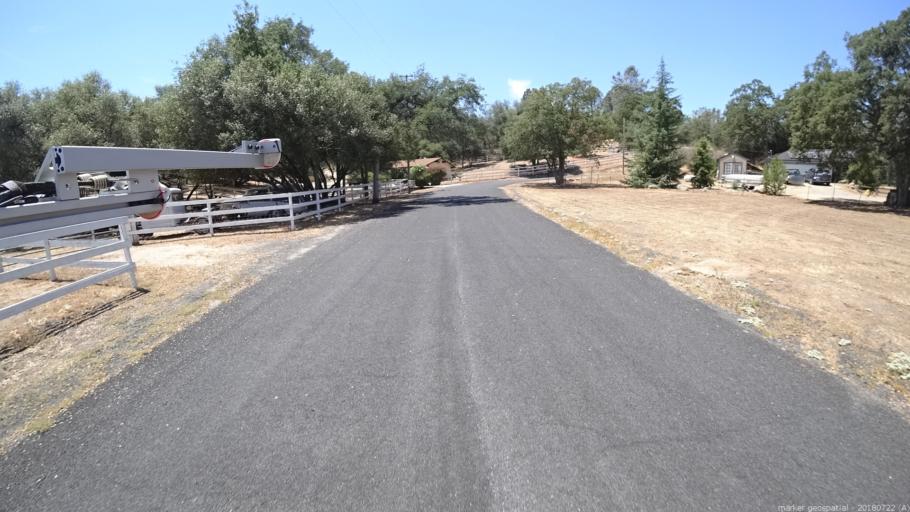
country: US
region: California
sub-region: Madera County
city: Yosemite Lakes
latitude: 37.2121
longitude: -119.7294
